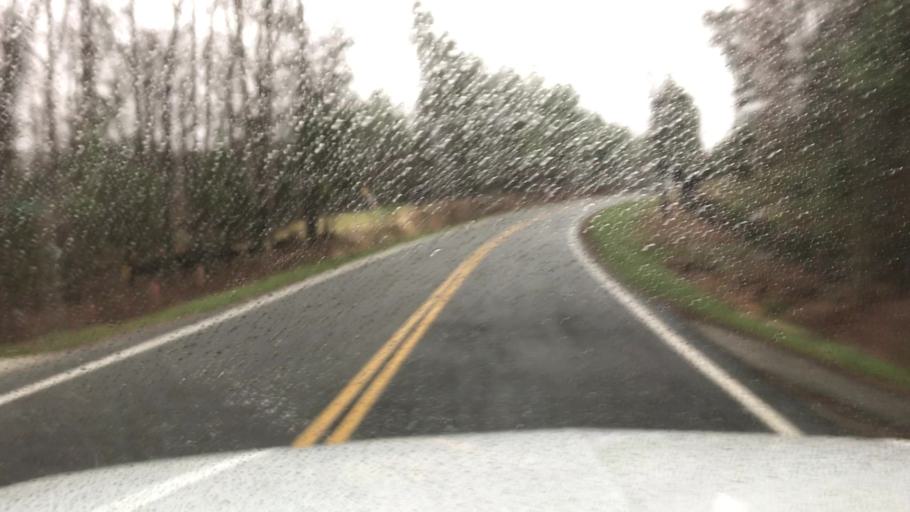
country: US
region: Virginia
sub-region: Henrico County
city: Short Pump
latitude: 37.6521
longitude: -77.6776
